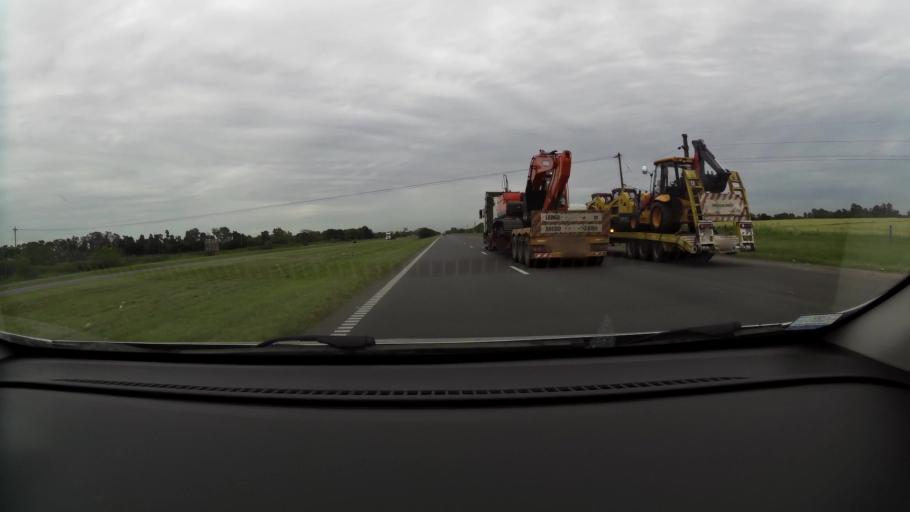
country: AR
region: Buenos Aires
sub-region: Partido de Zarate
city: Zarate
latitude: -34.0957
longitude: -59.1660
